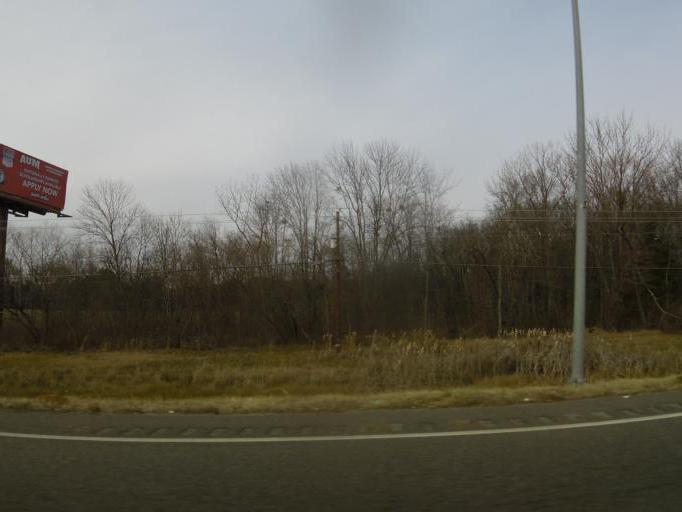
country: US
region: Alabama
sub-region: Montgomery County
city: Montgomery
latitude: 32.3361
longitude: -86.2286
